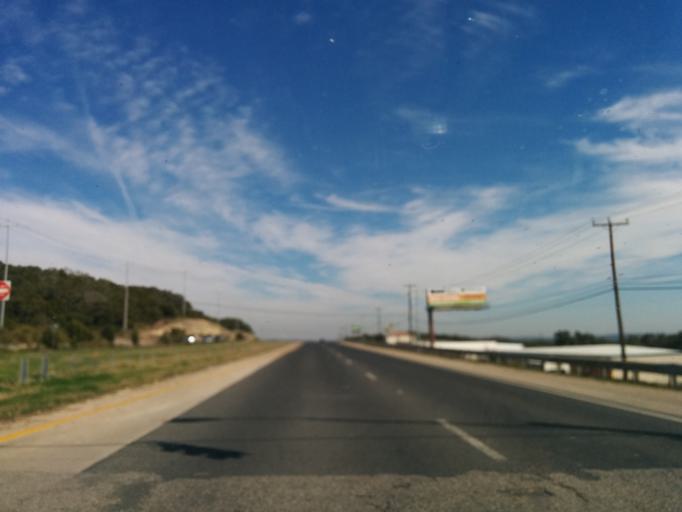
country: US
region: Texas
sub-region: Bexar County
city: Timberwood Park
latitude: 29.7101
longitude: -98.4485
